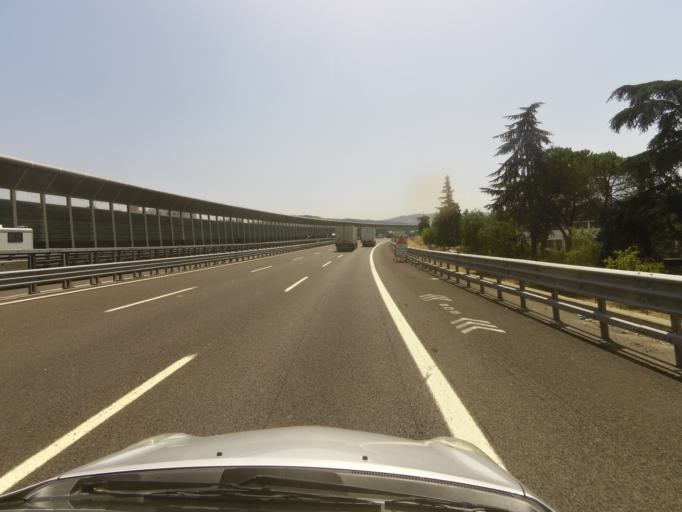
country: IT
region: Emilia-Romagna
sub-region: Provincia di Bologna
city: Casalecchio di Reno
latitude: 44.4701
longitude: 11.2731
